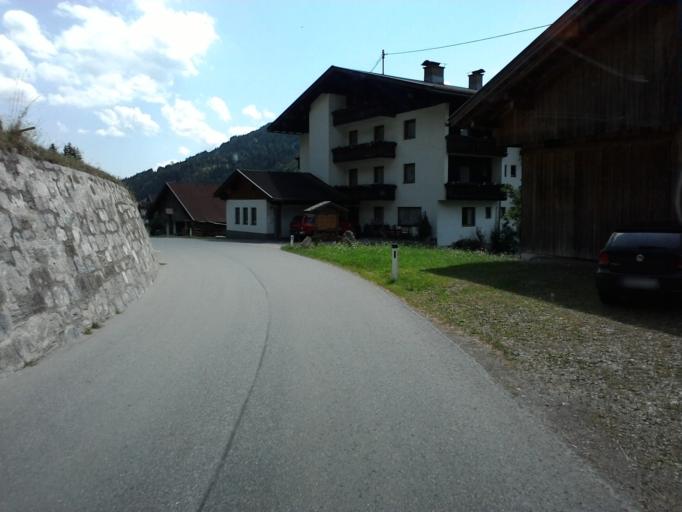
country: AT
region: Tyrol
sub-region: Politischer Bezirk Lienz
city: Untertilliach
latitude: 46.7038
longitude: 12.7427
